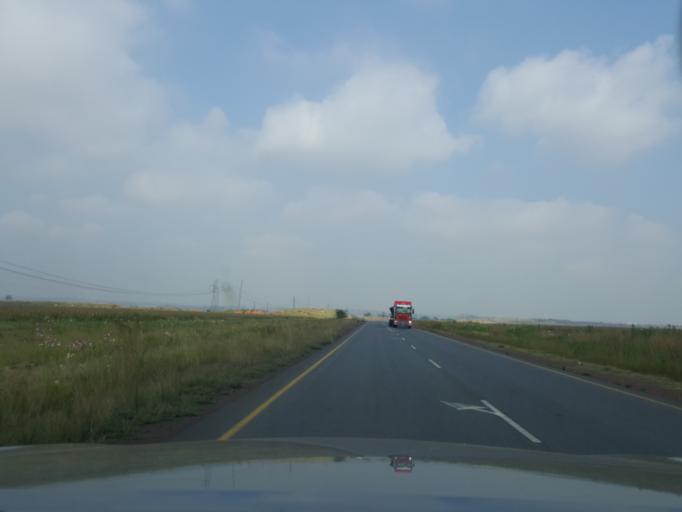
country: ZA
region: Mpumalanga
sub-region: Nkangala District Municipality
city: Witbank
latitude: -26.0144
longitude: 29.4073
